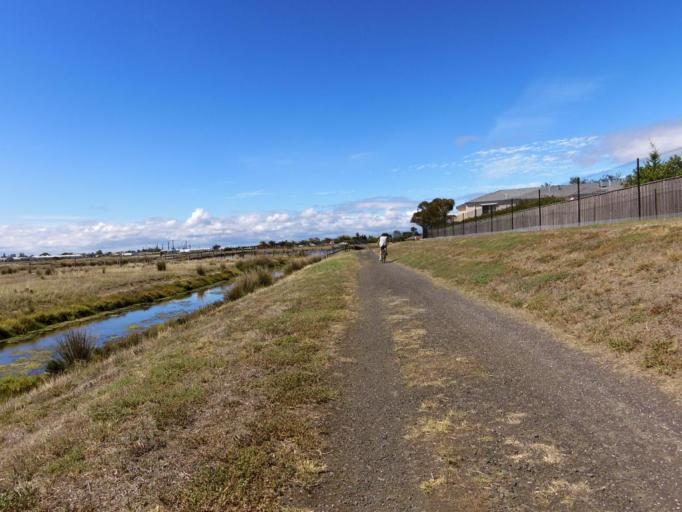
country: AU
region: Victoria
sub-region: Hobsons Bay
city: Altona Meadows
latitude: -37.8714
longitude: 144.8027
